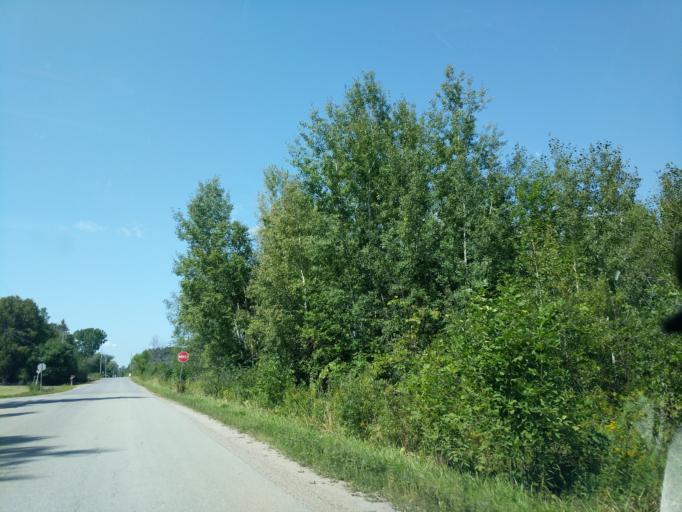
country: CA
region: Ontario
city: Bells Corners
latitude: 45.4467
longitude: -75.9106
